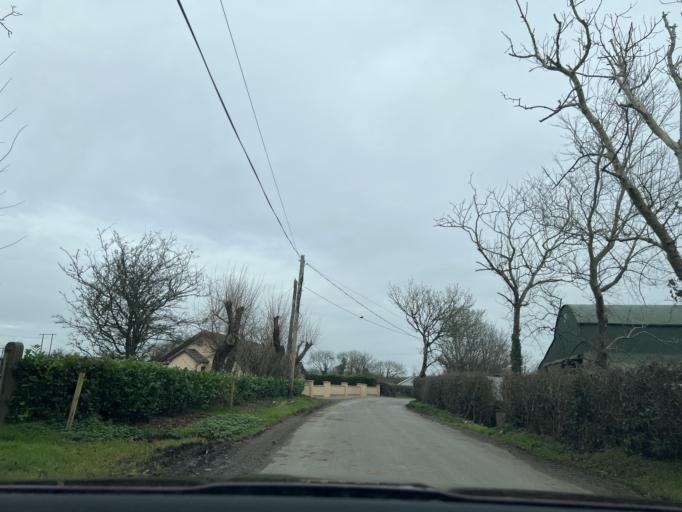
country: IE
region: Leinster
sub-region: Loch Garman
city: Castlebridge
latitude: 52.3787
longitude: -6.5251
